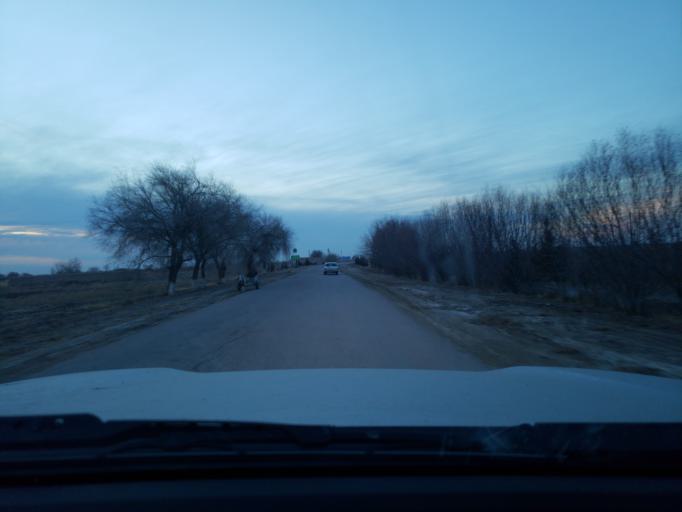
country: TM
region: Dasoguz
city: Tagta
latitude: 41.5856
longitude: 60.0546
